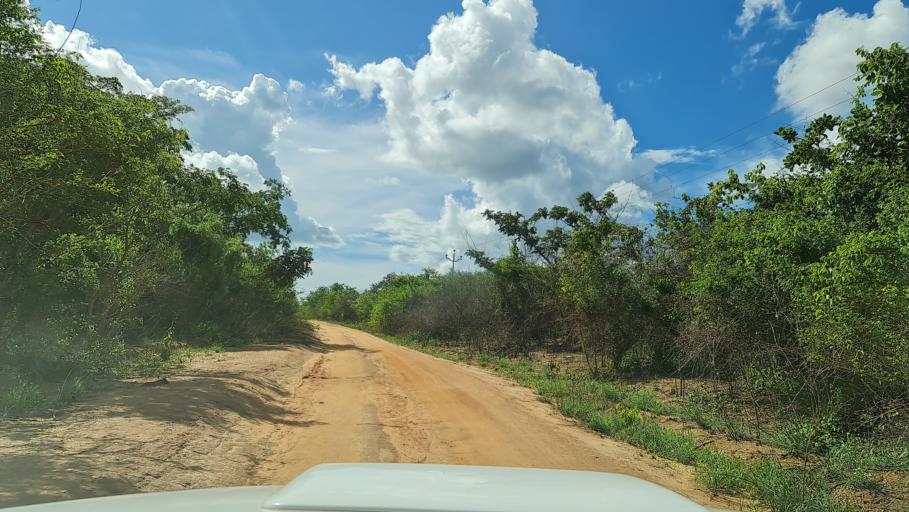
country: MZ
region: Nampula
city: Ilha de Mocambique
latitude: -15.4130
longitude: 40.2547
